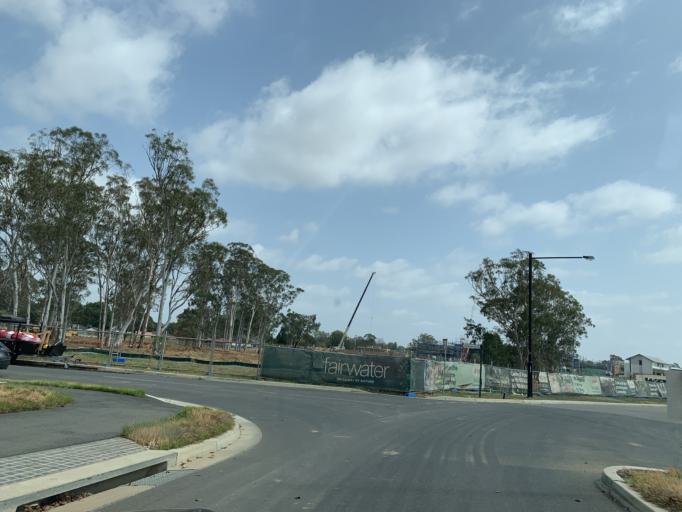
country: AU
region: New South Wales
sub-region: Blacktown
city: Blacktown
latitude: -33.7568
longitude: 150.9016
